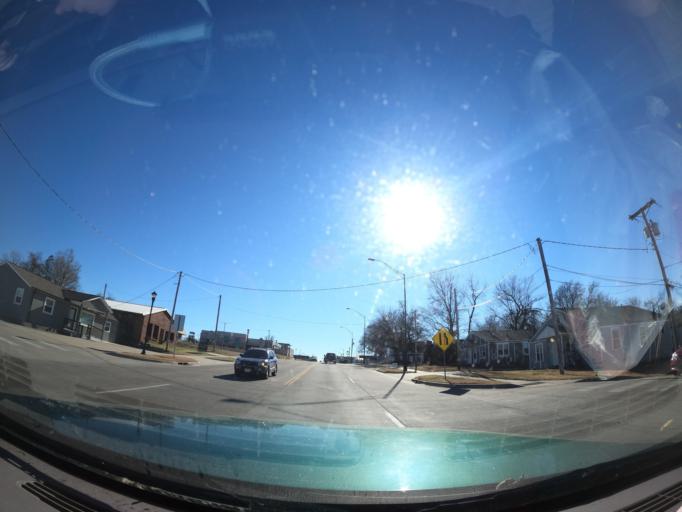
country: US
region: Oklahoma
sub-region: Wagoner County
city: Coweta
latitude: 35.9551
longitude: -95.6505
